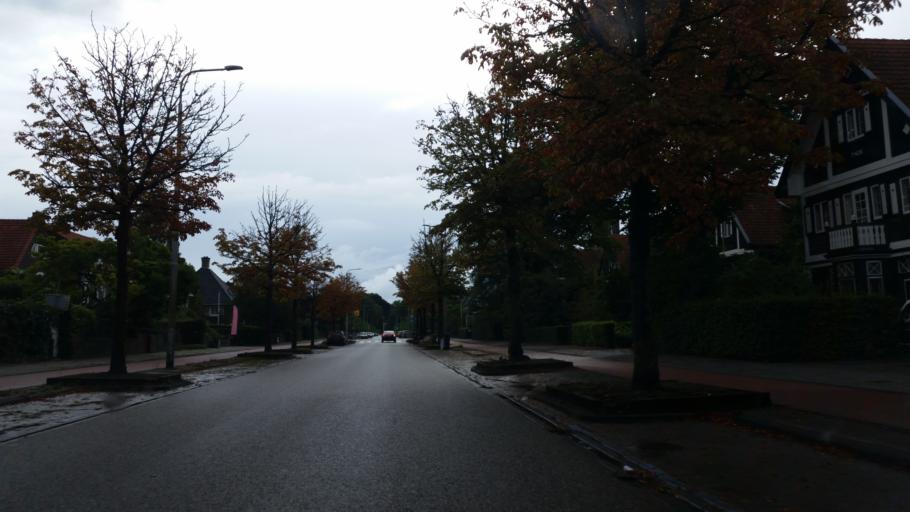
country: NL
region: Friesland
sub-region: Gemeente Leeuwarden
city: Bilgaard
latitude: 53.2045
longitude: 5.7810
